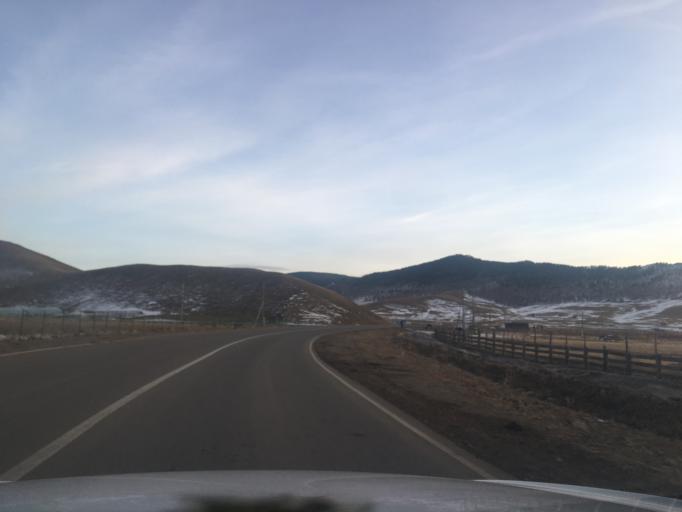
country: MN
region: Ulaanbaatar
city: Ulaanbaatar
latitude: 48.1023
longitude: 106.7367
